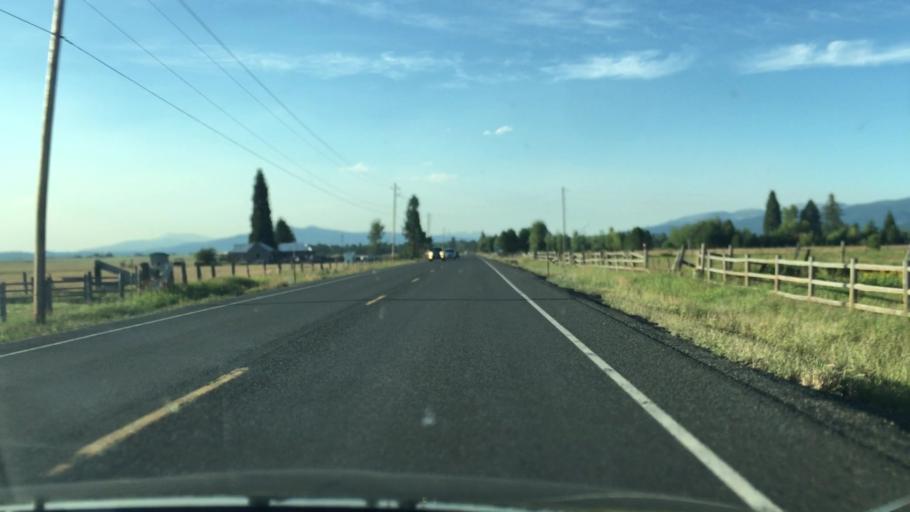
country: US
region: Idaho
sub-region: Valley County
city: McCall
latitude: 44.8106
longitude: -116.0781
